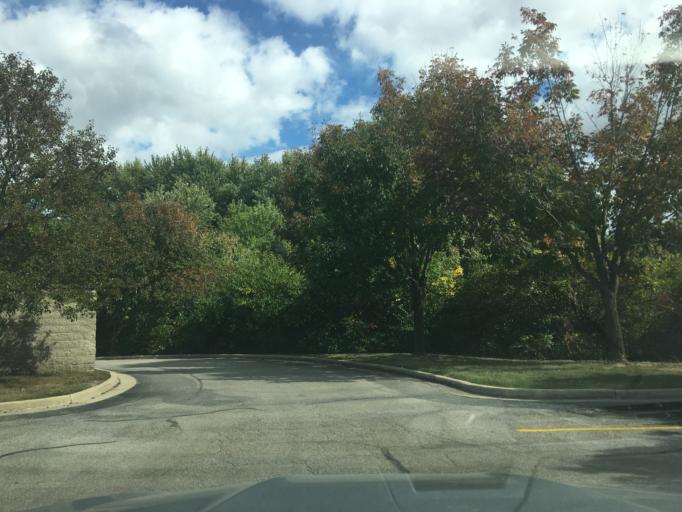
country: US
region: Indiana
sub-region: Tippecanoe County
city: West Lafayette
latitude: 40.4205
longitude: -86.9033
